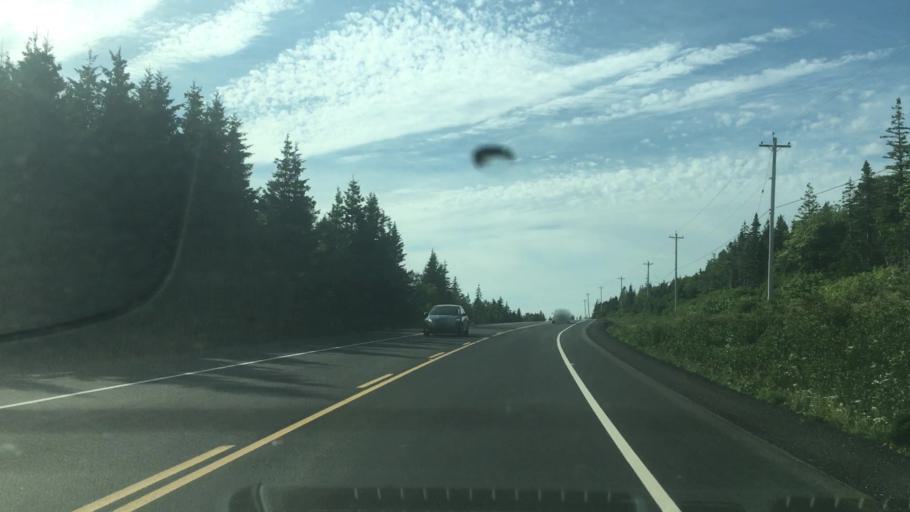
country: CA
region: Nova Scotia
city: Sydney Mines
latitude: 46.8435
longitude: -60.4029
